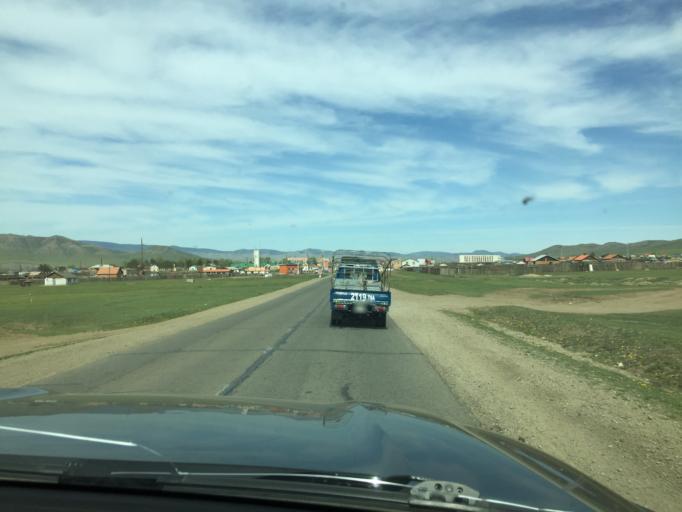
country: MN
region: Central Aimak
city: Ihsueuej
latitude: 48.2194
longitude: 106.3020
